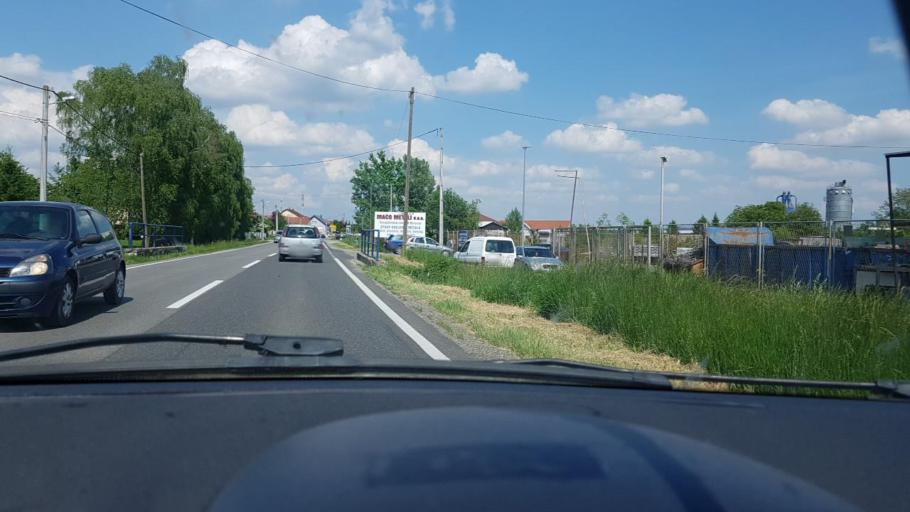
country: HR
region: Grad Zagreb
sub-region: Sesvete
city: Sesvete
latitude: 45.8797
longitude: 16.1699
